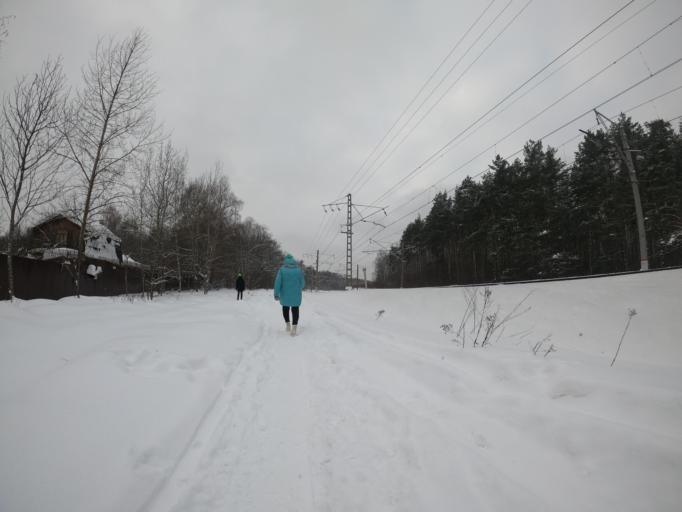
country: RU
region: Moskovskaya
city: Vostryakovo
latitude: 55.4164
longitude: 37.8258
